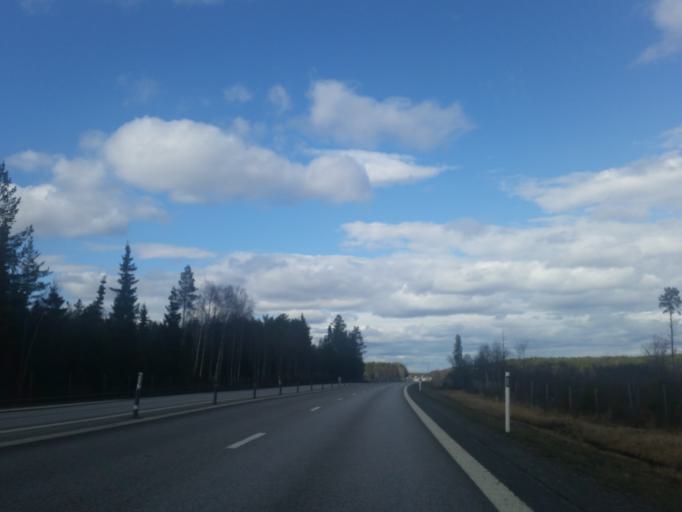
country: SE
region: Vaesterbotten
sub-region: Robertsfors Kommun
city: Robertsfors
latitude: 64.1237
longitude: 20.8840
